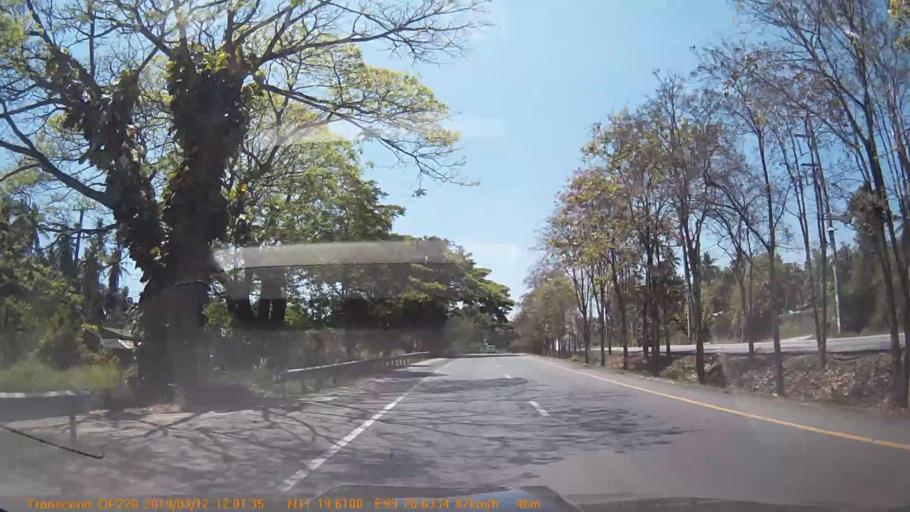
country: TH
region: Prachuap Khiri Khan
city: Bang Saphan
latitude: 11.3266
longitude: 99.4771
